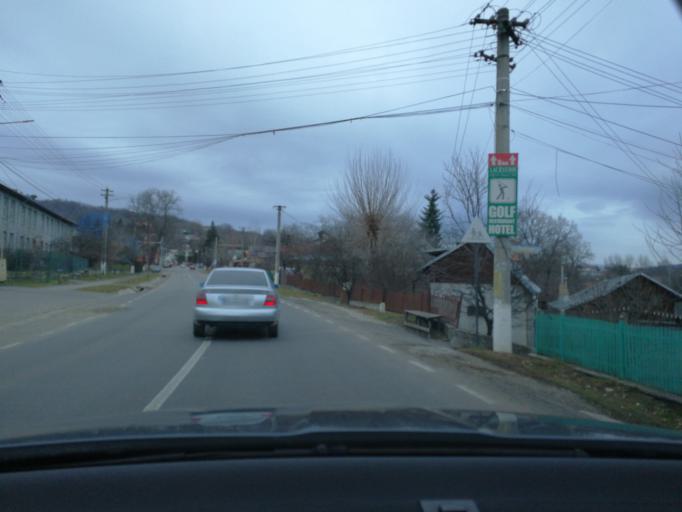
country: RO
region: Prahova
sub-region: Comuna Cornu
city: Cornu de Jos
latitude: 45.1484
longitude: 25.6917
